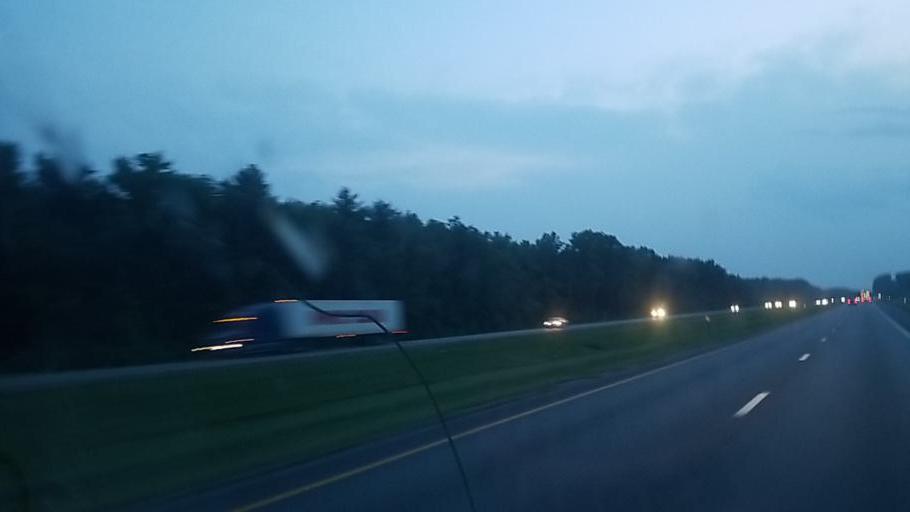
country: US
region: New York
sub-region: Madison County
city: Bolivar
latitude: 43.0920
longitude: -75.9422
